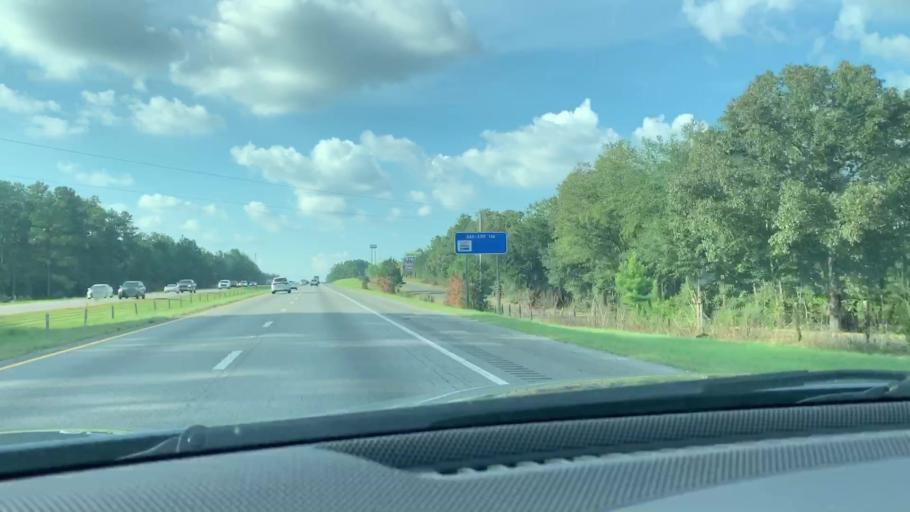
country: US
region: South Carolina
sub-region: Calhoun County
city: Saint Matthews
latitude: 33.6663
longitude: -80.8934
